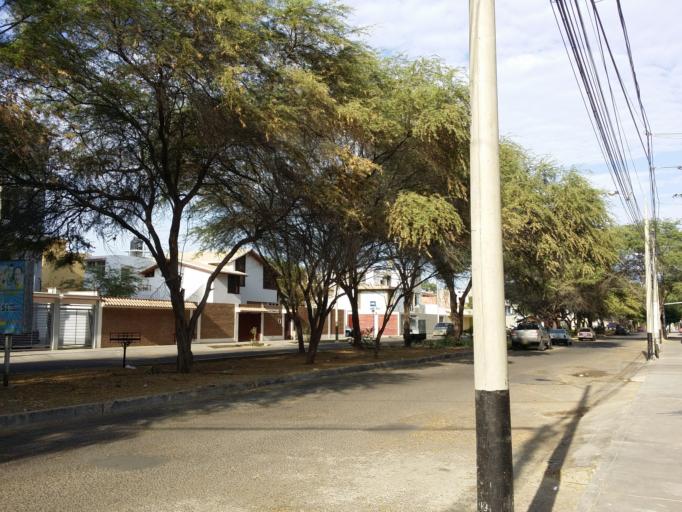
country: PE
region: Piura
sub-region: Provincia de Piura
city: Piura
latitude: -5.1720
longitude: -80.6284
